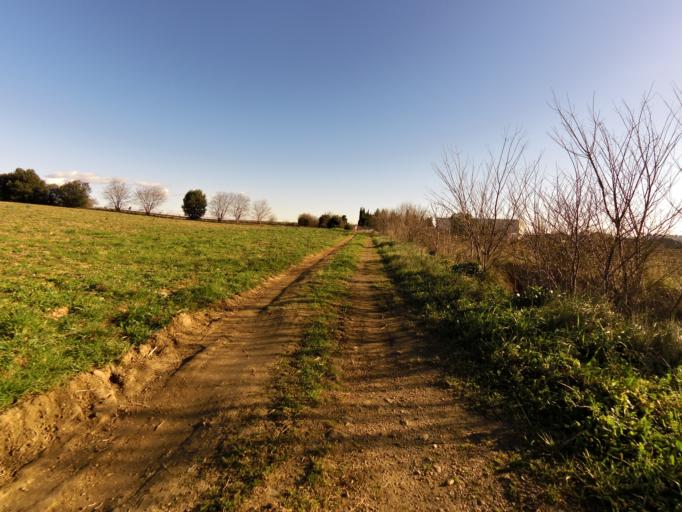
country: FR
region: Languedoc-Roussillon
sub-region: Departement du Gard
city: Mus
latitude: 43.7308
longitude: 4.1939
